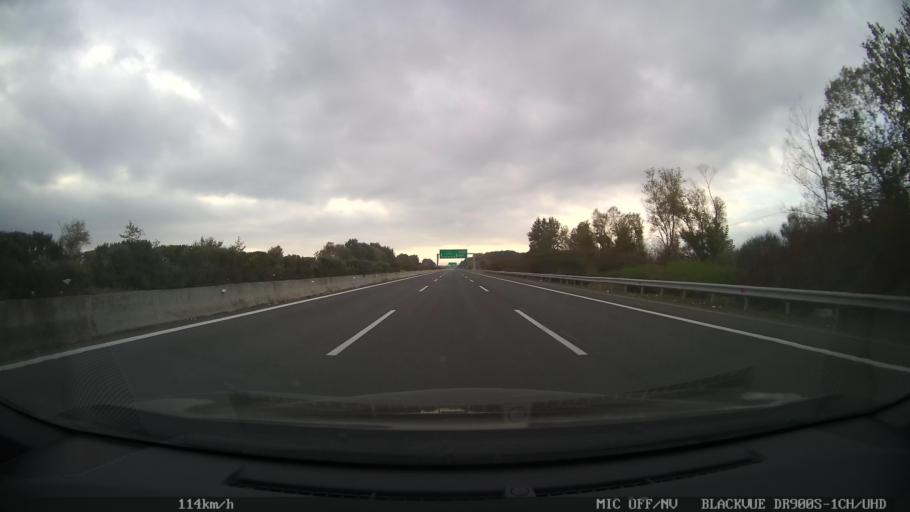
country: GR
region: Central Macedonia
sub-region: Nomos Pierias
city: Nea Efesos
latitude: 40.2086
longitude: 22.5448
